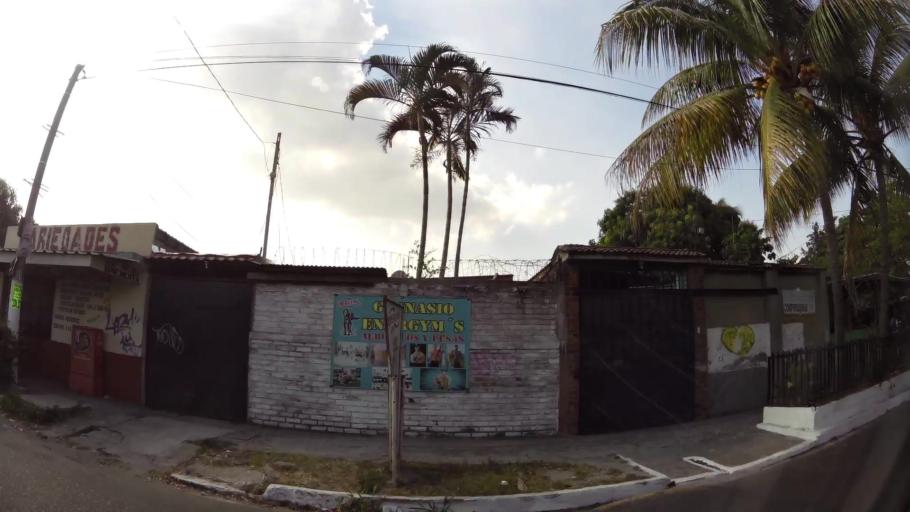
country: SV
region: San Salvador
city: Soyapango
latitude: 13.7184
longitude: -89.1274
